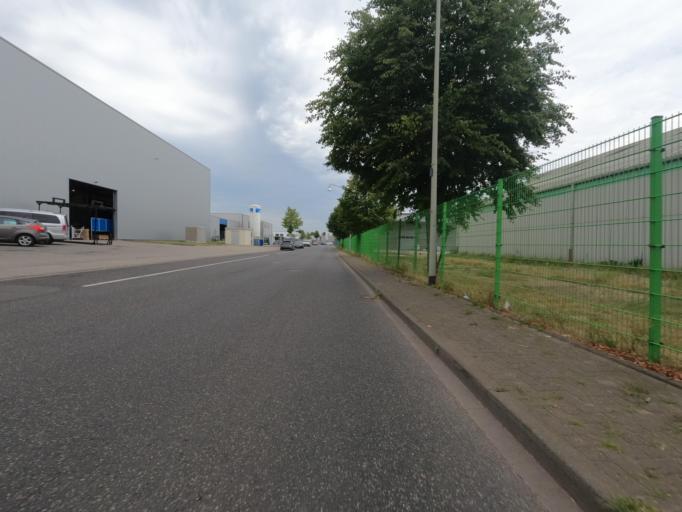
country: DE
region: North Rhine-Westphalia
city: Geilenkirchen
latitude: 50.9749
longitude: 6.0963
